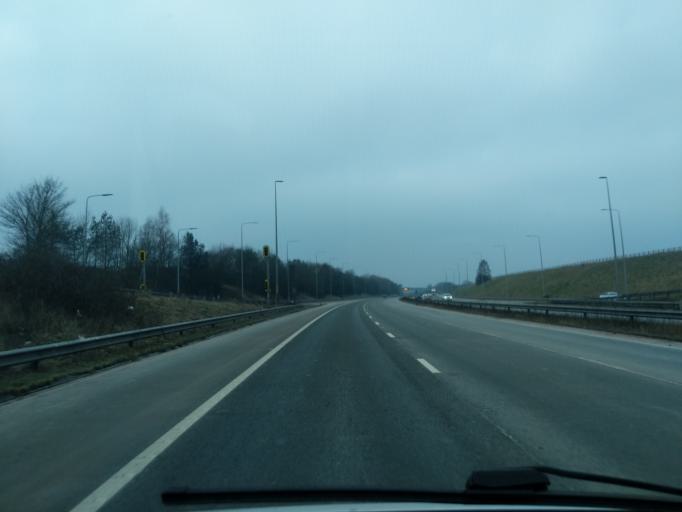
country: GB
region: England
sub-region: Warrington
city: Winwick
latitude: 53.4410
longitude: -2.5856
